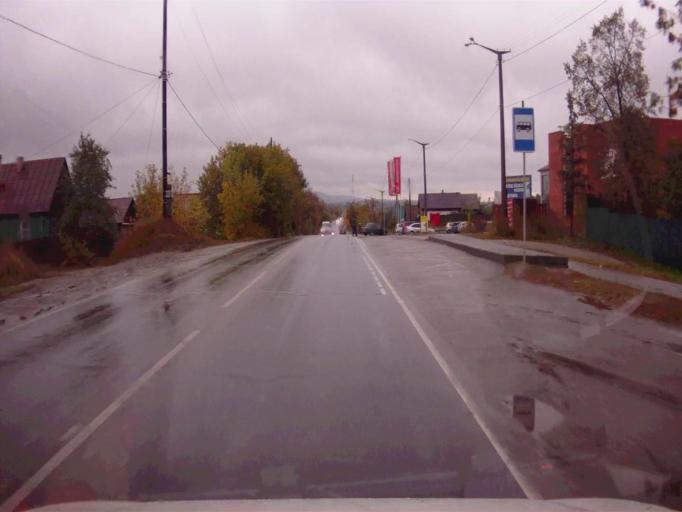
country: RU
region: Chelyabinsk
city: Kyshtym
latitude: 55.7076
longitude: 60.5568
